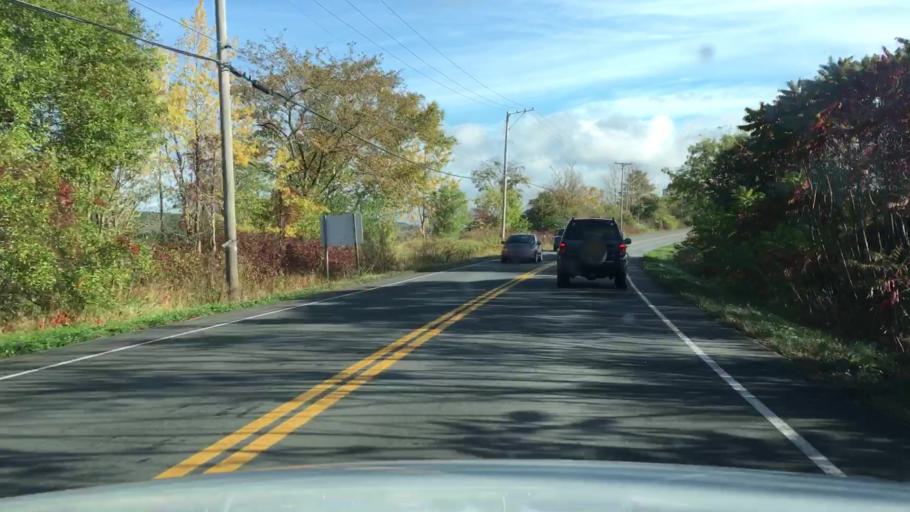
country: US
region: Maine
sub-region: Knox County
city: Thomaston
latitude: 44.0967
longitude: -69.1517
